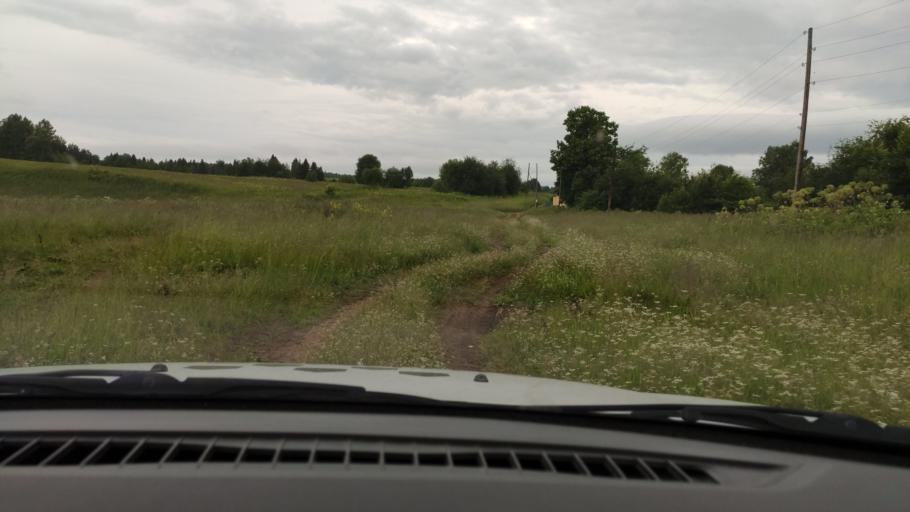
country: RU
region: Perm
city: Orda
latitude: 57.2912
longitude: 56.5904
